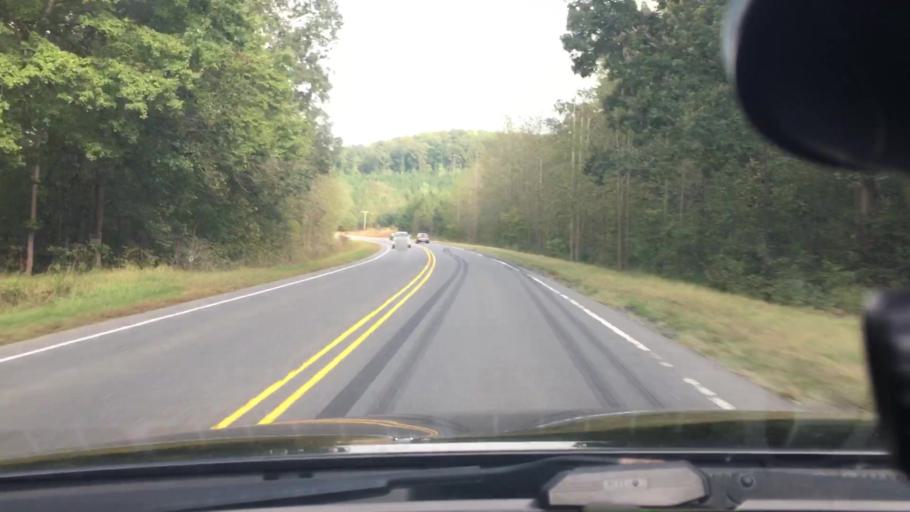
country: US
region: North Carolina
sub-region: Montgomery County
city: Mount Gilead
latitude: 35.3026
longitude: -80.0274
